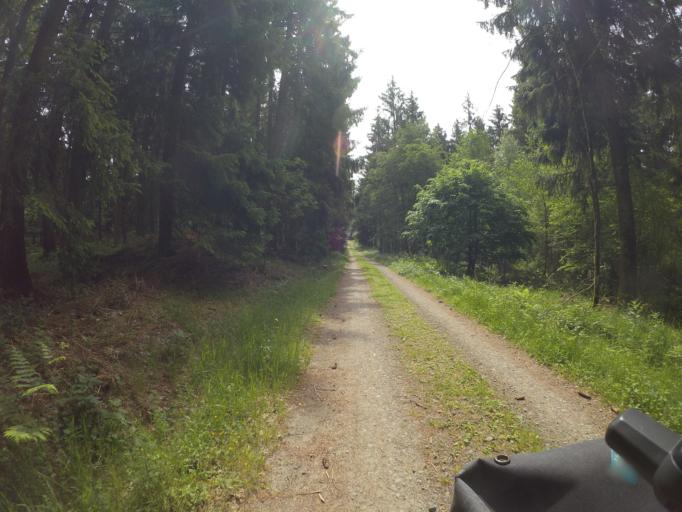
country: DE
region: Rheinland-Pfalz
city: Damflos
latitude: 49.6822
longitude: 6.9740
